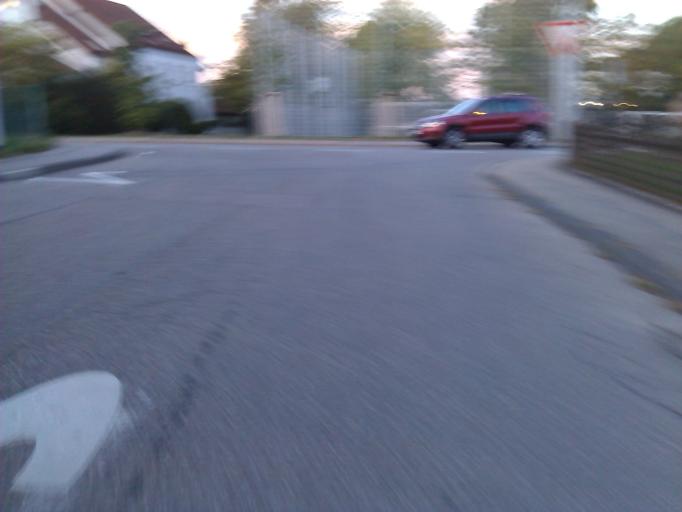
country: DE
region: Baden-Wuerttemberg
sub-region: Regierungsbezirk Stuttgart
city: Talheim
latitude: 49.1139
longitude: 9.1699
